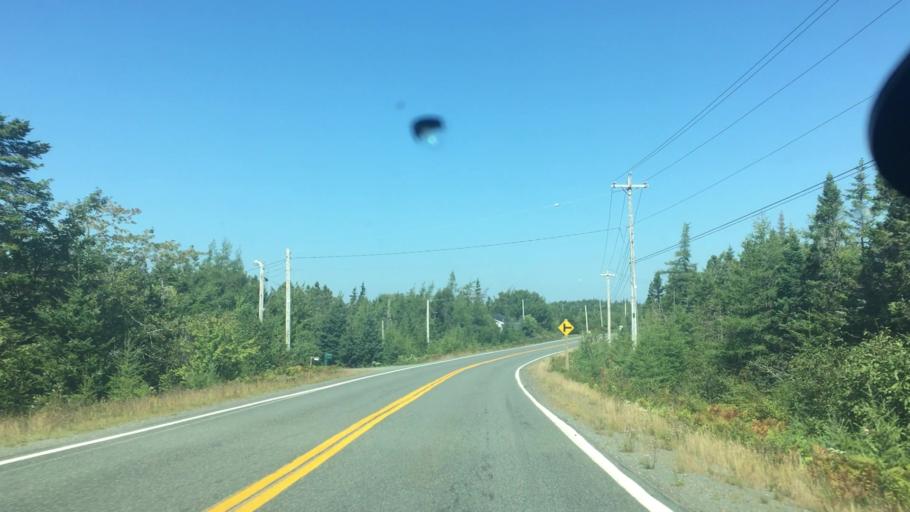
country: CA
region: Nova Scotia
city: Antigonish
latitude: 44.9966
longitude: -62.0994
